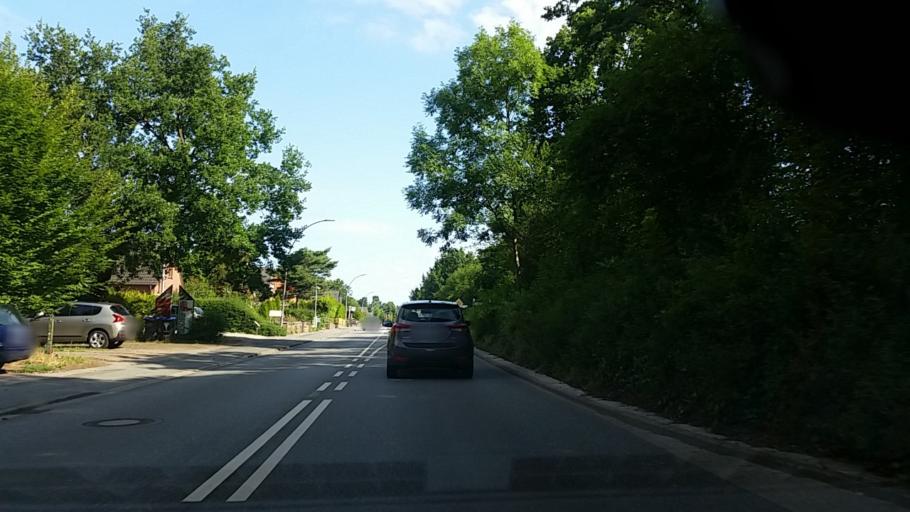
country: DE
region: Hamburg
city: Langenhorn
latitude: 53.6895
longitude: 10.0297
